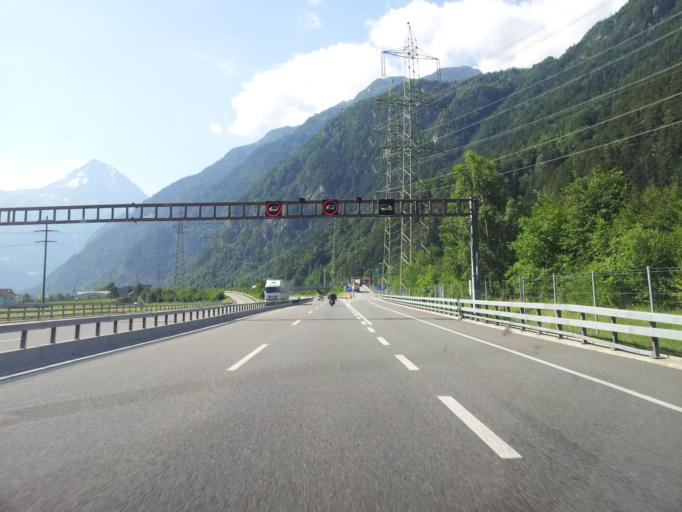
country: CH
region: Uri
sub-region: Uri
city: Erstfeld
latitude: 46.8376
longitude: 8.6369
